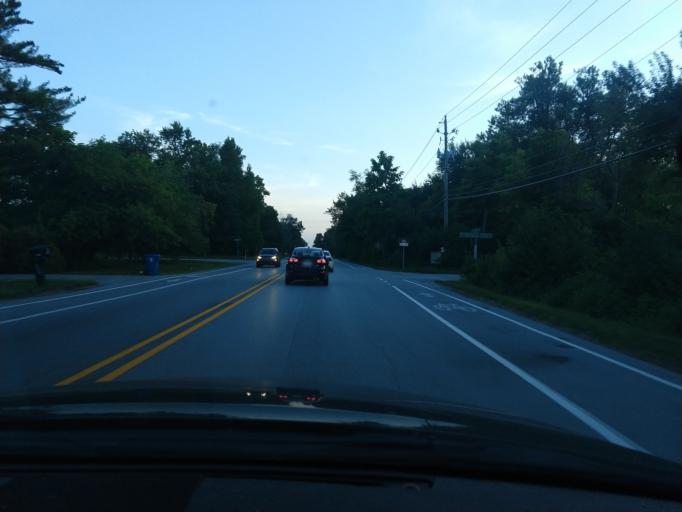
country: US
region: Indiana
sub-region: Marion County
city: Broad Ripple
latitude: 39.8655
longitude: -86.0986
